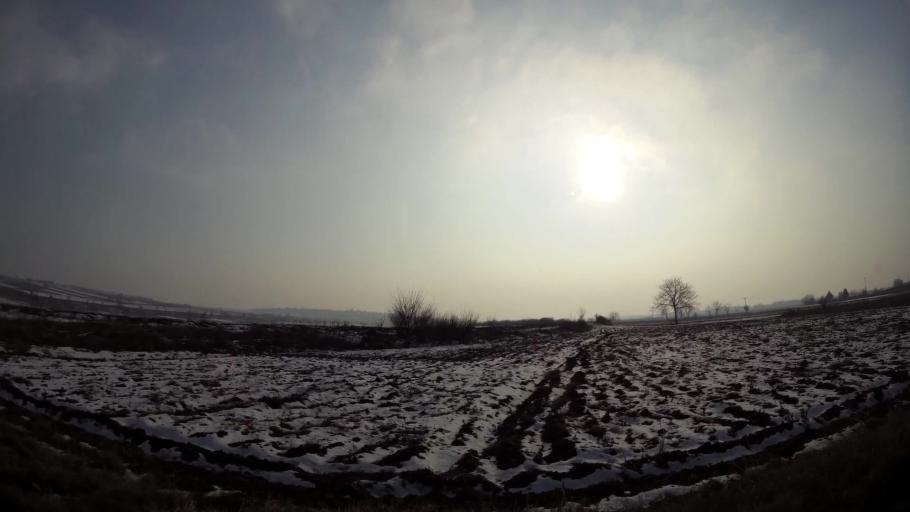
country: MK
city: Miladinovci
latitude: 41.9739
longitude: 21.6426
